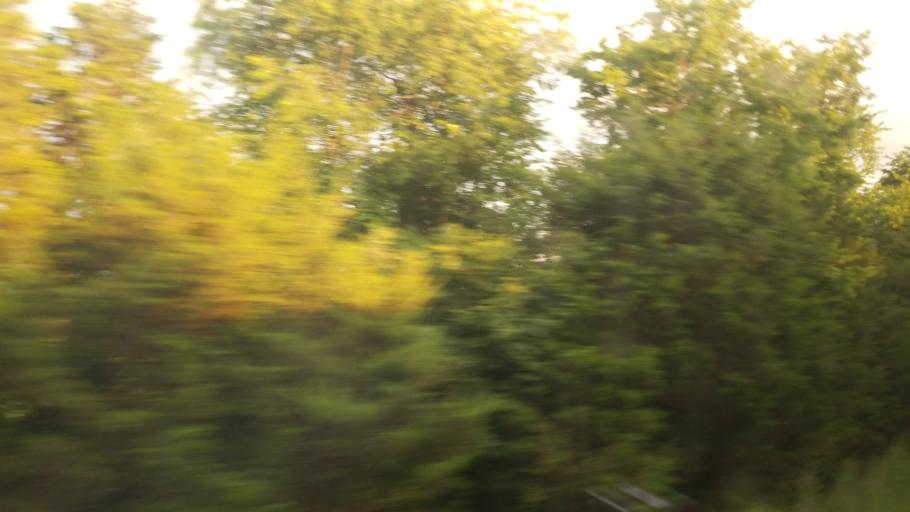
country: US
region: Virginia
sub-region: Prince William County
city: Nokesville
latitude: 38.6364
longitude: -77.6661
